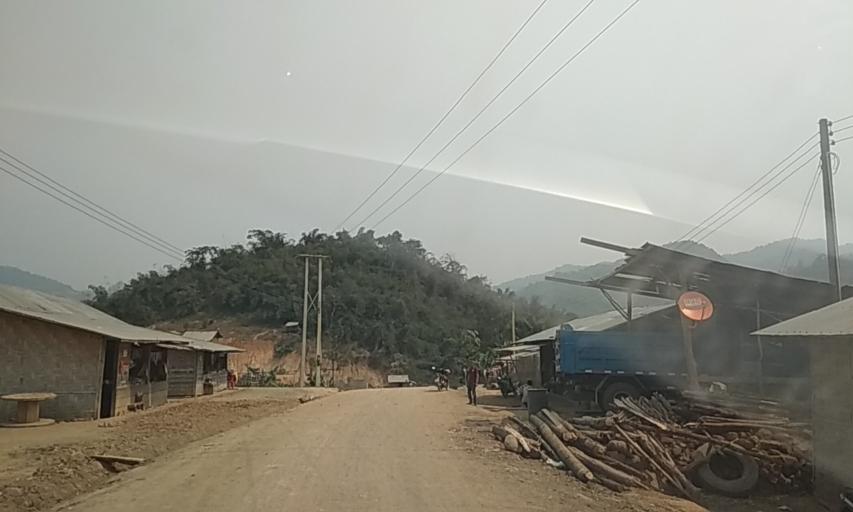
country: VN
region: Huyen Dien Bien
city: Dien Bien Phu
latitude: 21.4237
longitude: 102.7621
